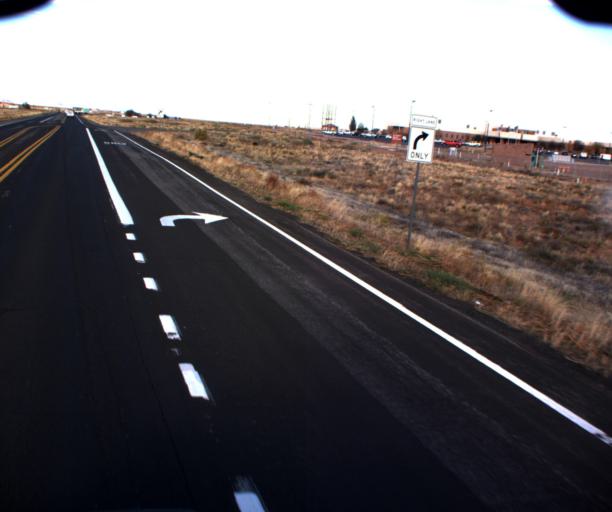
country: US
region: Arizona
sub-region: Apache County
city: Lukachukai
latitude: 36.9597
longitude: -109.3461
